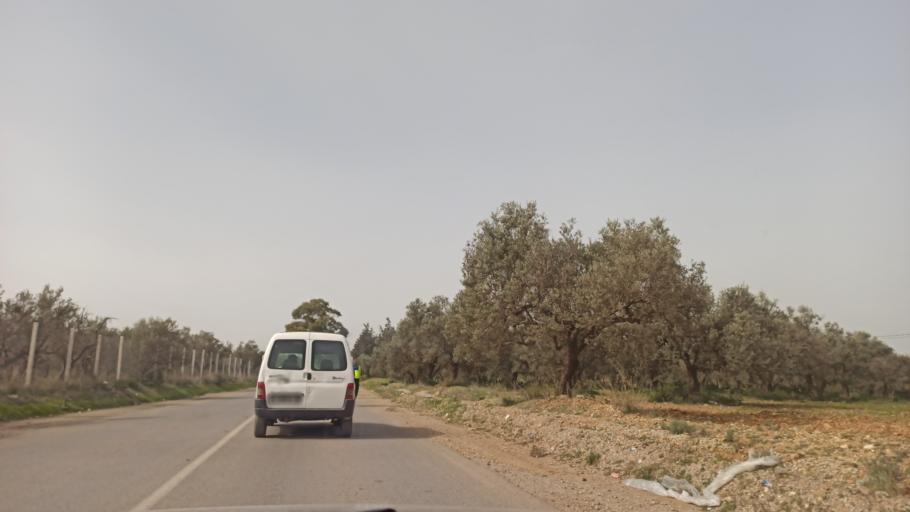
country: TN
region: Zaghwan
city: Zaghouan
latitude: 36.4187
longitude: 10.1112
